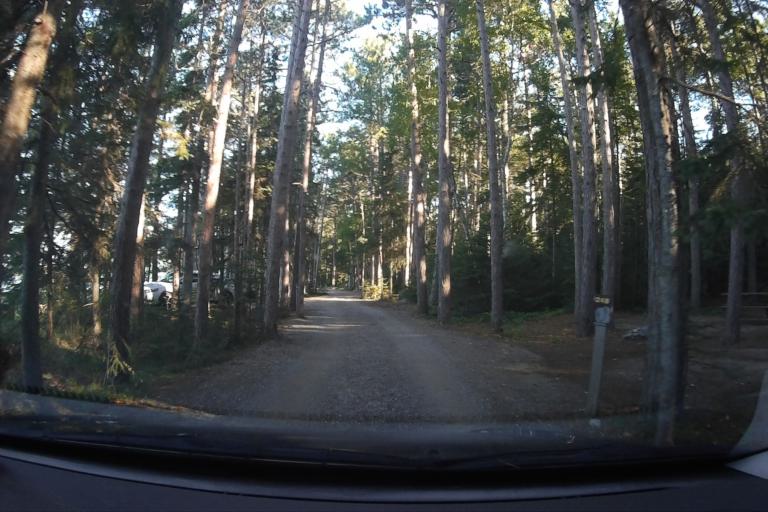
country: CA
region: Ontario
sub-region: Algoma
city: Sault Ste. Marie
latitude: 47.3256
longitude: -84.6112
